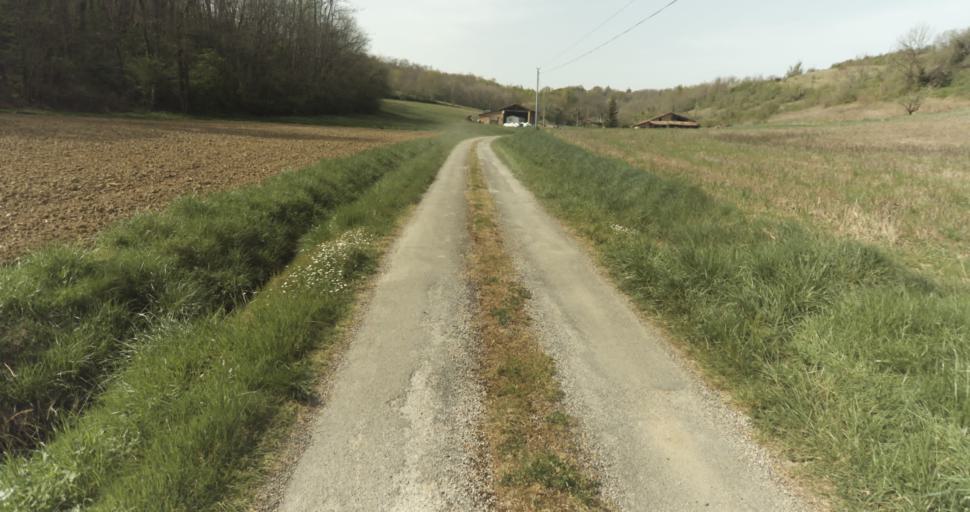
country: FR
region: Midi-Pyrenees
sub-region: Departement du Tarn-et-Garonne
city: Moissac
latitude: 44.1363
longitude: 1.1508
